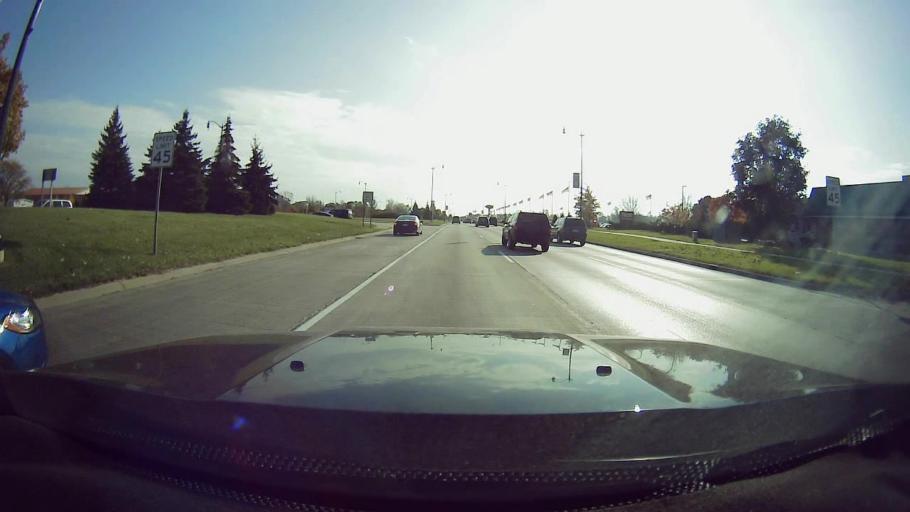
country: US
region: Michigan
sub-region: Wayne County
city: Taylor
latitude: 42.2109
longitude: -83.2689
